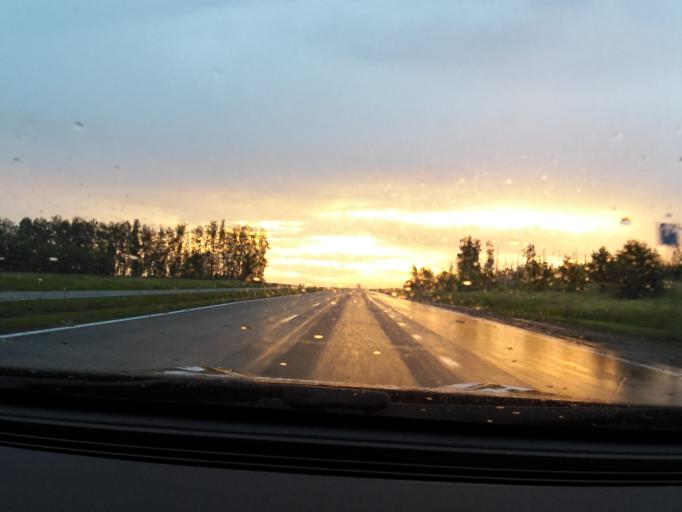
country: RU
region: Tatarstan
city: Yelabuga
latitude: 55.7857
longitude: 52.1692
